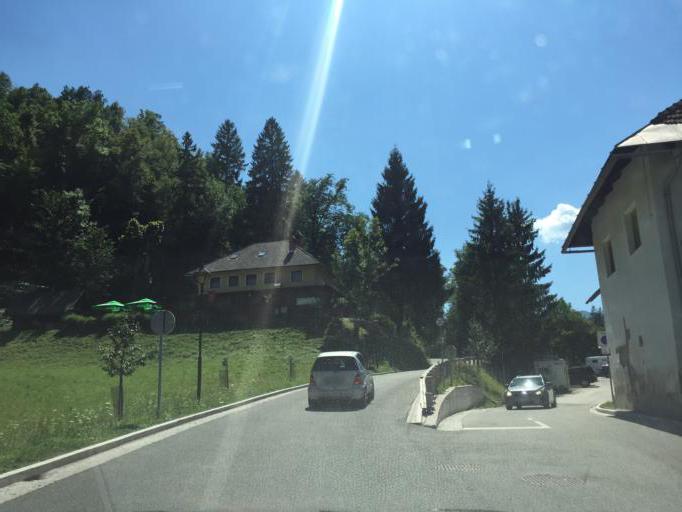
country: SI
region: Bled
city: Bled
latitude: 46.3712
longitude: 14.0989
